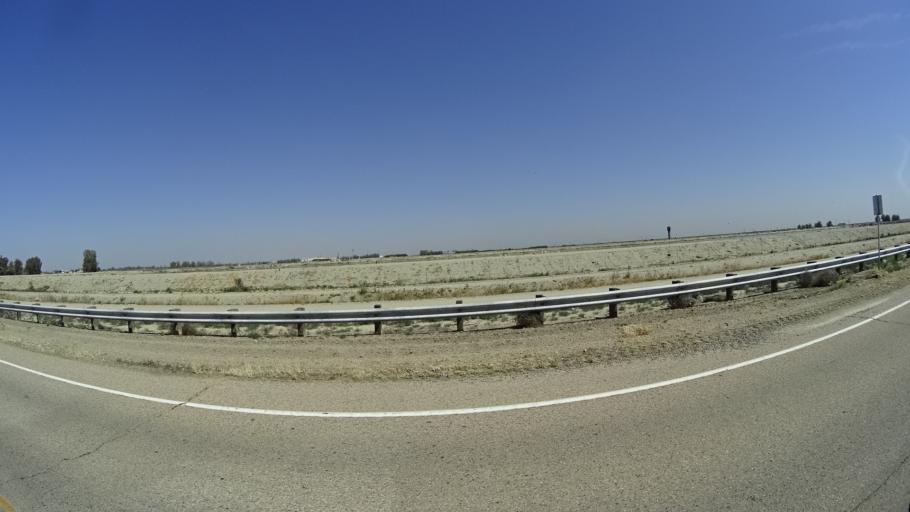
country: US
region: California
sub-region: Kings County
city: Corcoran
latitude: 36.0649
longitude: -119.5438
